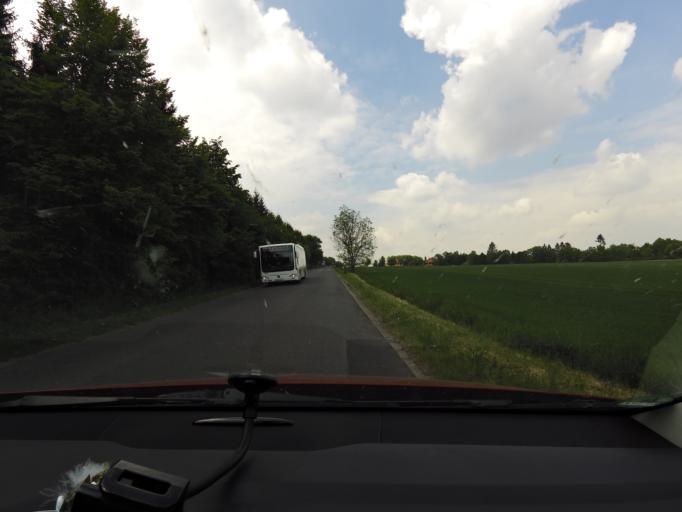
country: DE
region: Thuringia
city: Oberdorla
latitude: 51.2037
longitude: 10.3974
